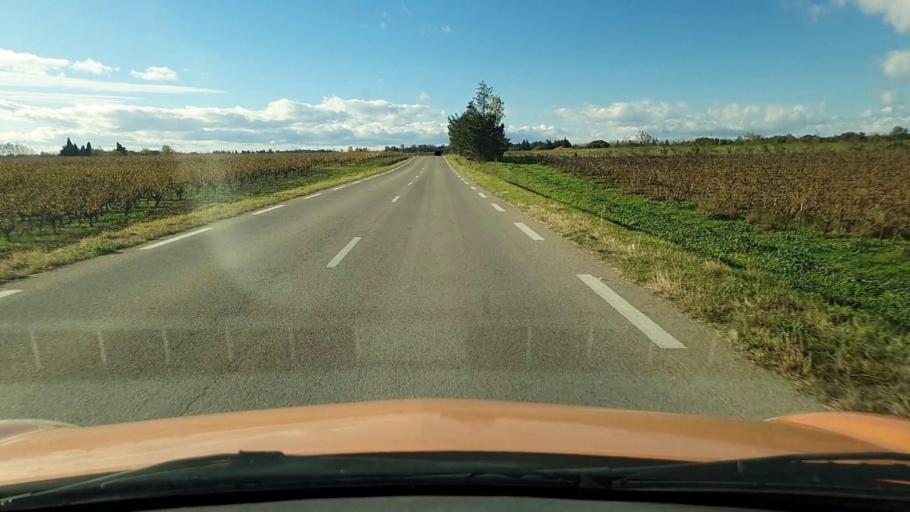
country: FR
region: Languedoc-Roussillon
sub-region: Departement du Gard
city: Vauvert
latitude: 43.6509
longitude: 4.3136
